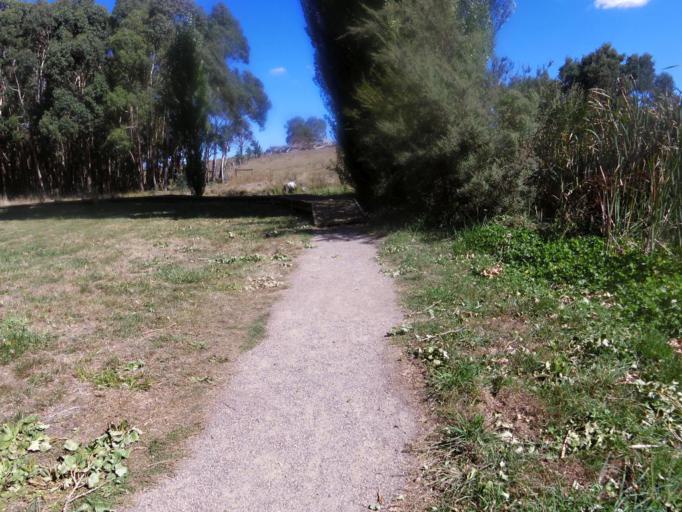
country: AU
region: Victoria
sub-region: Mount Alexander
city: Castlemaine
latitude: -37.2507
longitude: 144.4440
